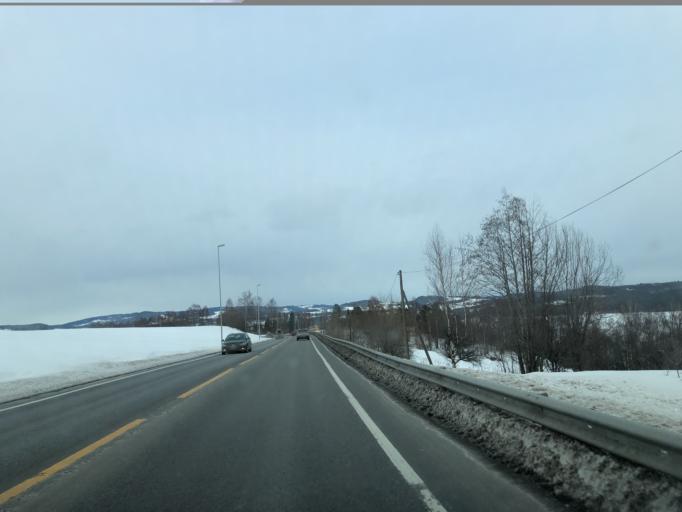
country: NO
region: Oppland
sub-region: Gjovik
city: Gjovik
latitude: 60.8544
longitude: 10.6940
